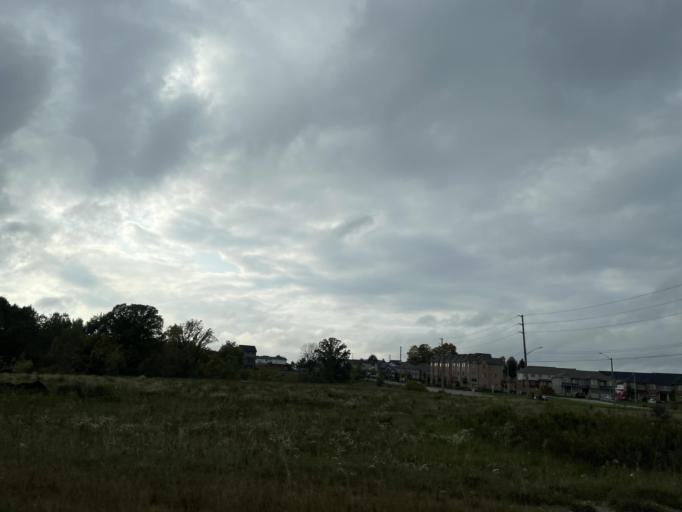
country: CA
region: Ontario
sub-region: Wellington County
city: Guelph
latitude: 43.5658
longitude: -80.2120
